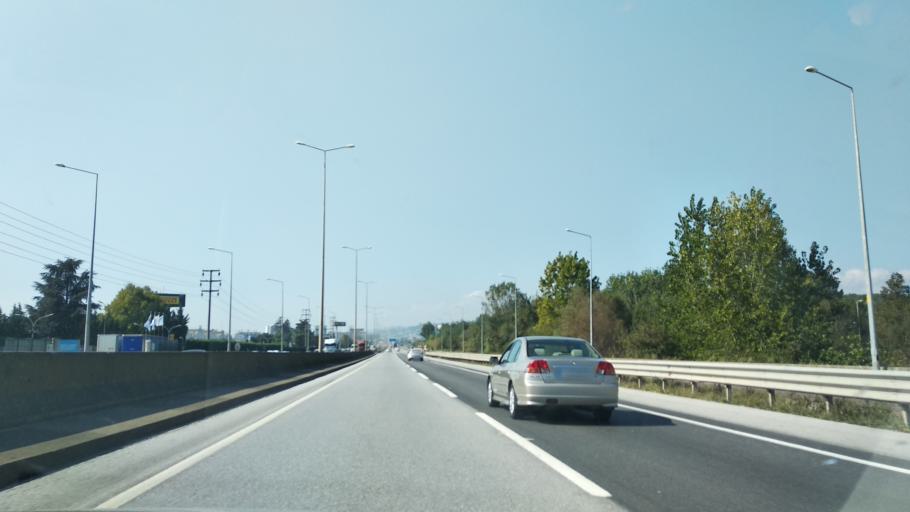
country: TR
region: Kocaeli
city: Kosekoy
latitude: 40.7565
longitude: 30.0031
